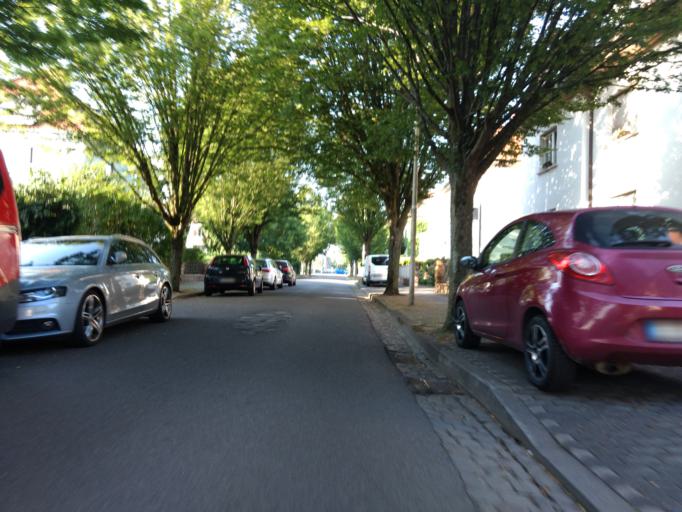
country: DE
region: Saarland
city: Saarlouis
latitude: 49.3099
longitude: 6.7438
